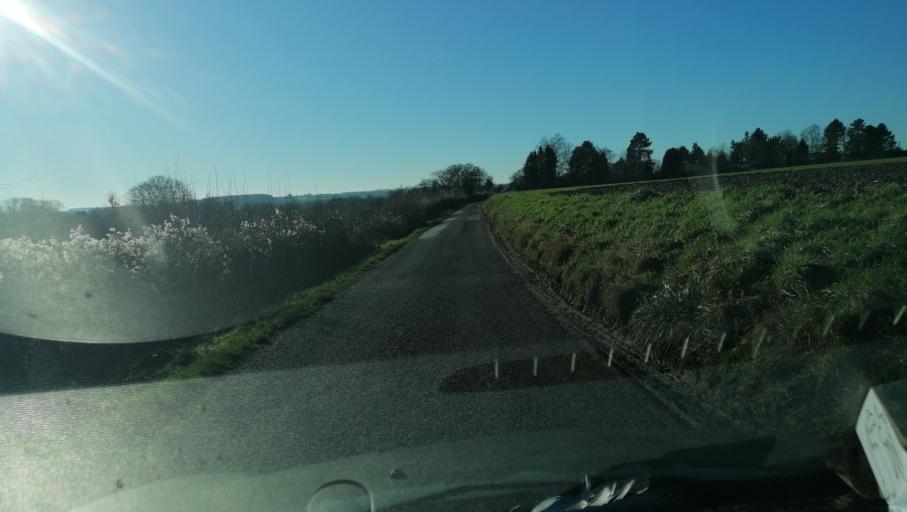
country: FR
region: Nord-Pas-de-Calais
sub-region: Departement du Nord
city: Ferriere-la-Grande
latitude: 50.2257
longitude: 4.0407
